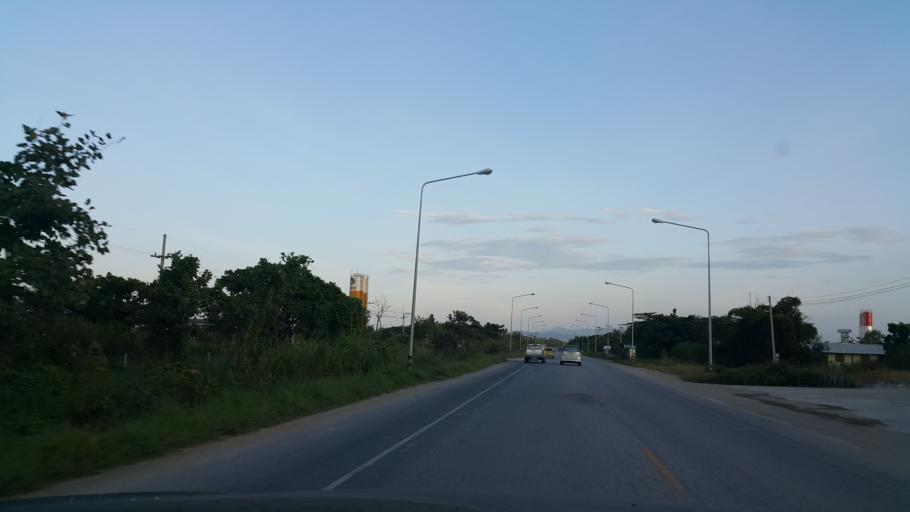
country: TH
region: Lamphun
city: Pa Sang
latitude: 18.5269
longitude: 98.8692
